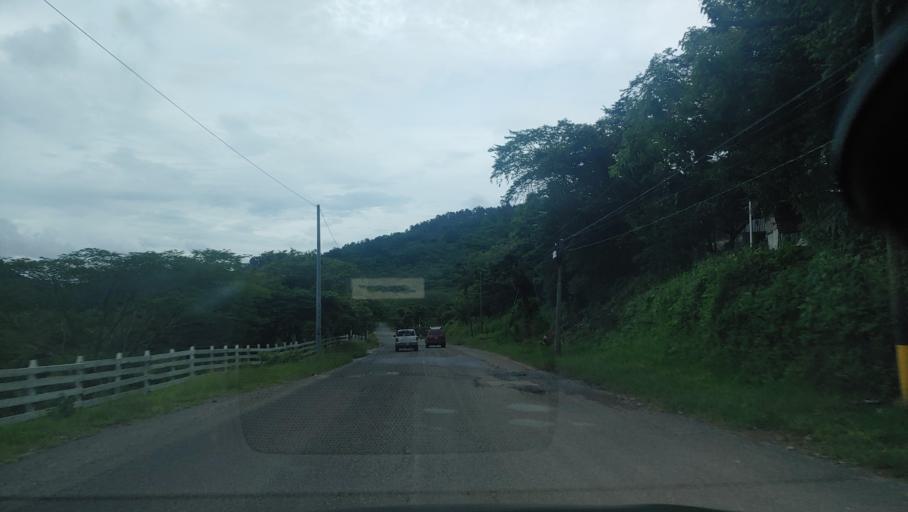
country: HN
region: Choluteca
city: San Marcos de Colon
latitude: 13.3803
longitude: -86.8713
